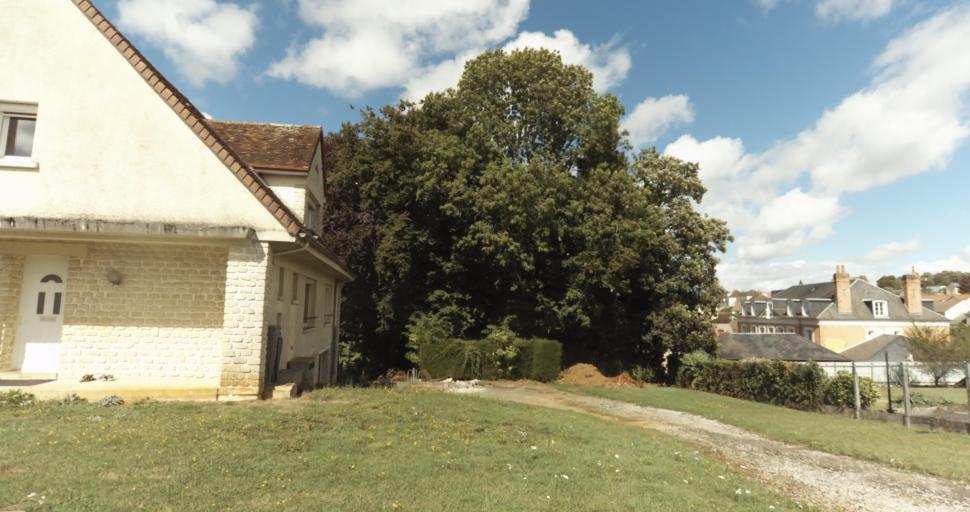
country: FR
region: Lower Normandy
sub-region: Departement de l'Orne
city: Gace
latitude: 48.7886
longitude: 0.2951
